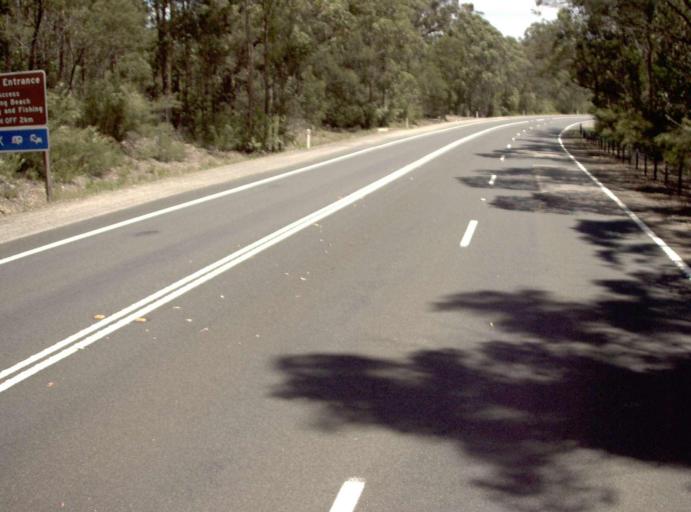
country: AU
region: Victoria
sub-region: East Gippsland
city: Lakes Entrance
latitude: -37.7317
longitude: 148.1120
